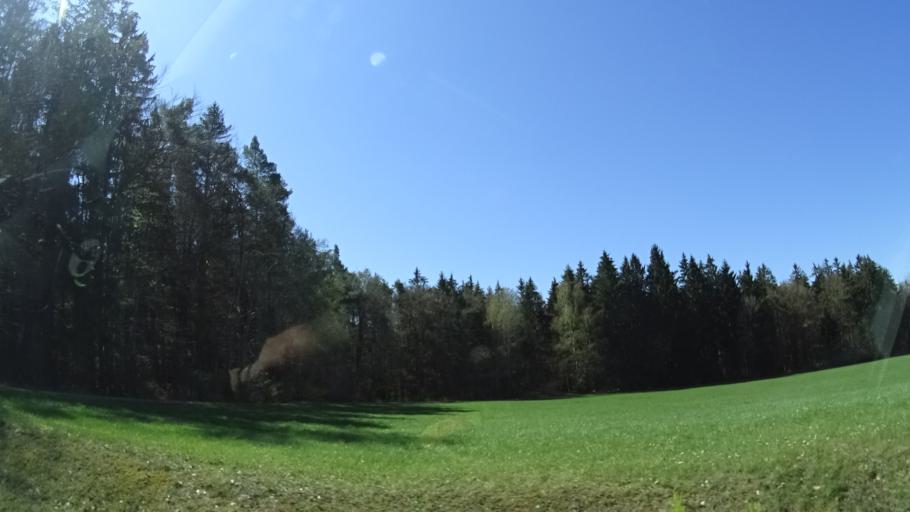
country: DE
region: Bavaria
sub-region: Upper Palatinate
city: Kastl
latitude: 49.4096
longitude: 11.6474
